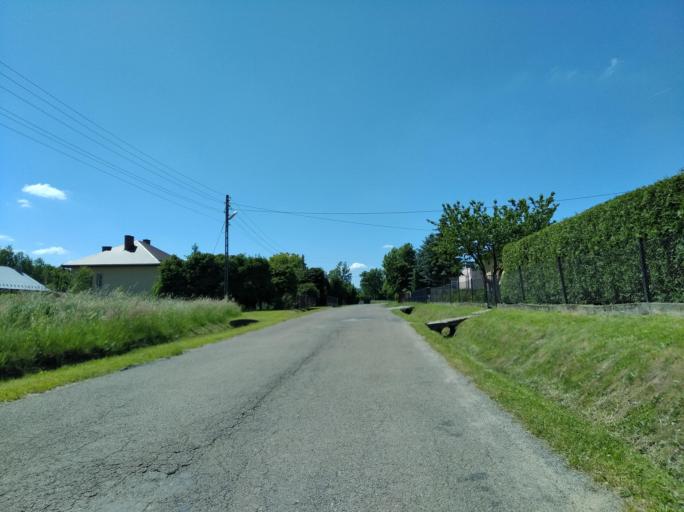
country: PL
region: Subcarpathian Voivodeship
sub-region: Powiat jasielski
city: Nowy Zmigrod
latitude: 49.6330
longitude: 21.5908
